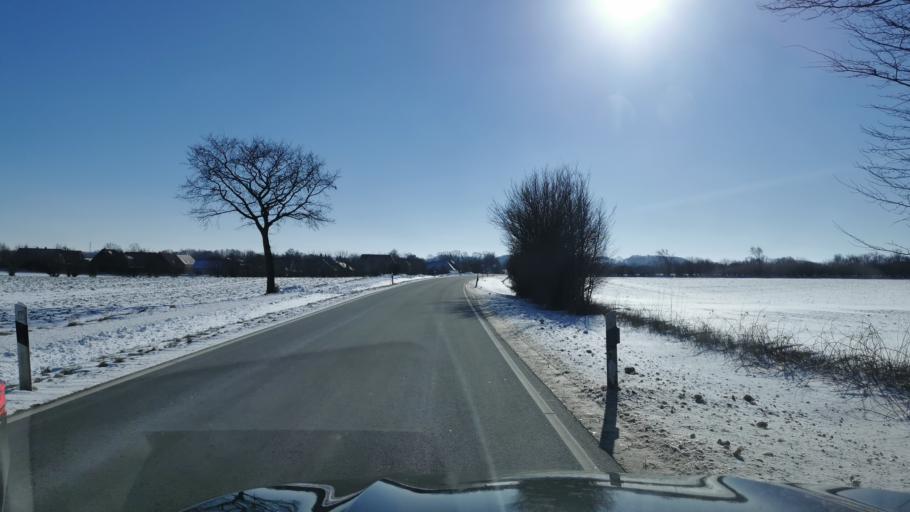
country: DE
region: Schleswig-Holstein
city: Langballig
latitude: 54.8097
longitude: 9.6382
